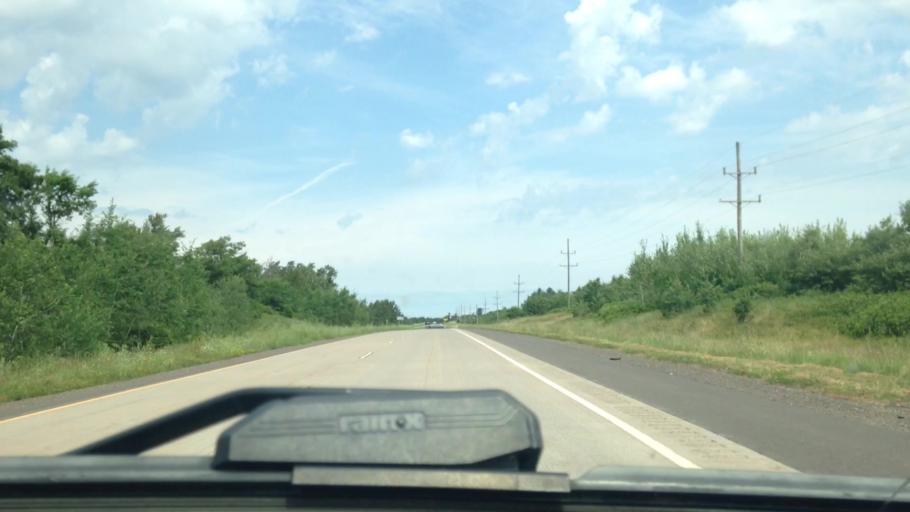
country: US
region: Wisconsin
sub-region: Douglas County
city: Lake Nebagamon
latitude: 46.2761
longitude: -91.8065
